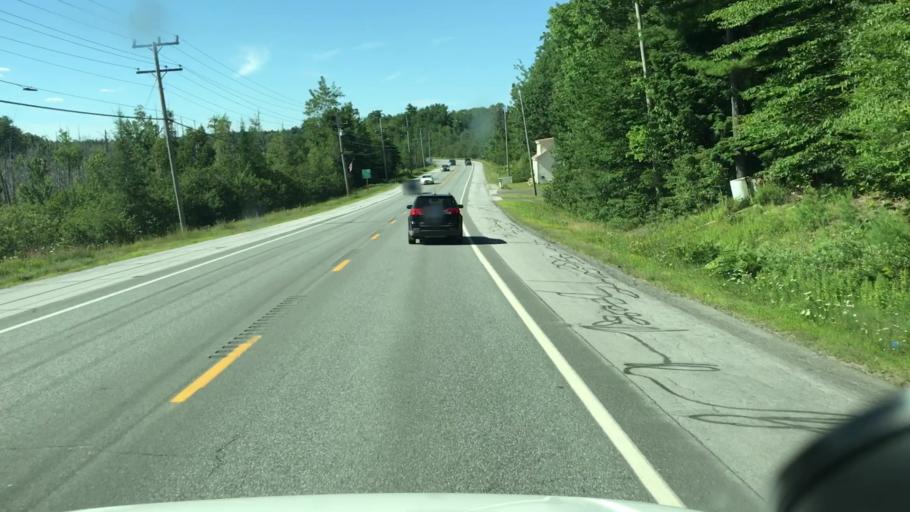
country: US
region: Maine
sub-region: Hancock County
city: Dedham
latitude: 44.7304
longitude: -68.6241
